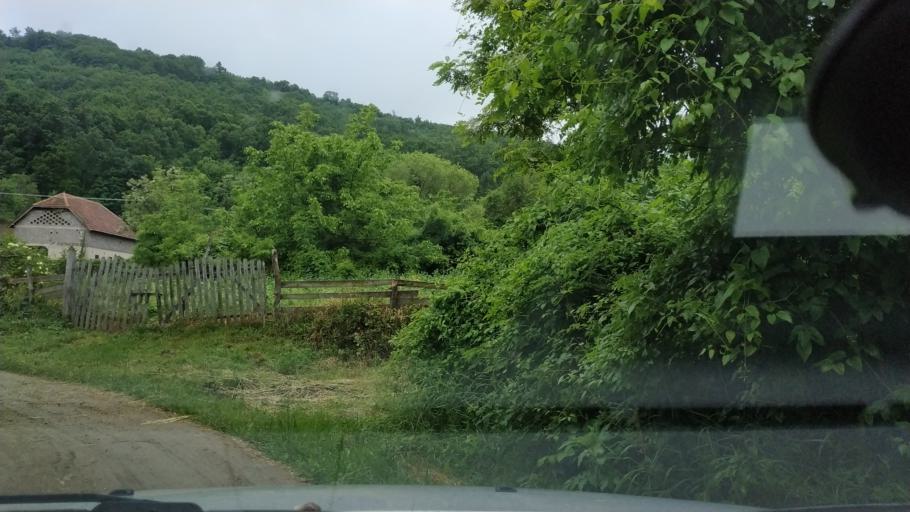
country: RS
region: Central Serbia
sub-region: Toplicki Okrug
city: Prokuplje
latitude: 43.3920
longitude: 21.5595
